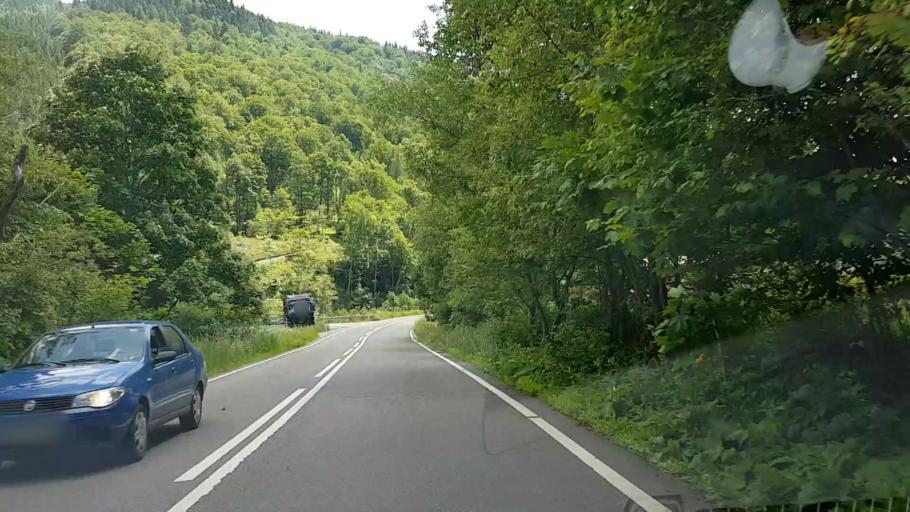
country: RO
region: Suceava
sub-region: Comuna Crucea
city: Crucea
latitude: 47.3226
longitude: 25.6254
